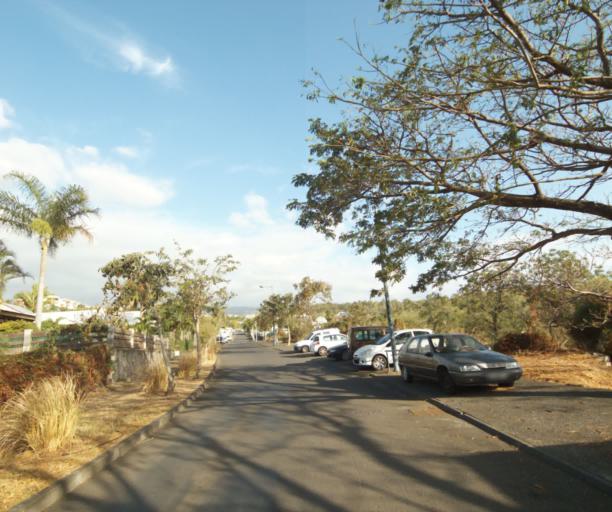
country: RE
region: Reunion
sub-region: Reunion
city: Saint-Paul
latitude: -21.0464
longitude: 55.2568
